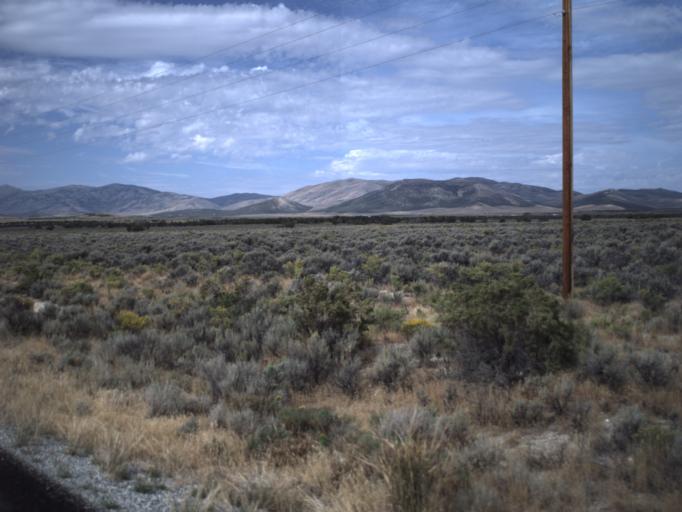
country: US
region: Idaho
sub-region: Cassia County
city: Burley
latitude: 41.7834
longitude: -113.4828
